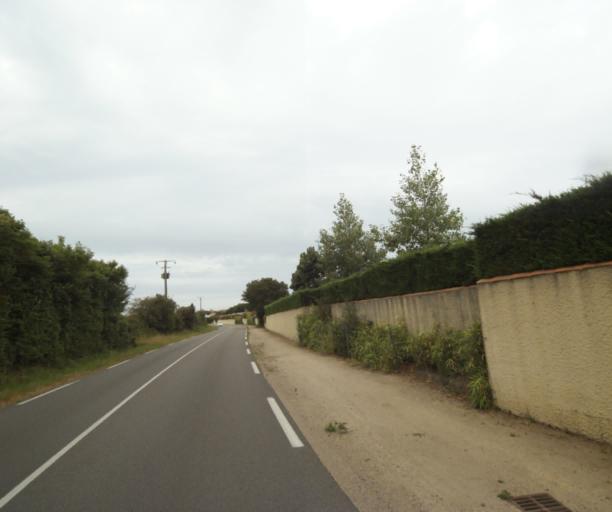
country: FR
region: Pays de la Loire
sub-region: Departement de la Vendee
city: Chateau-d'Olonne
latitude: 46.4724
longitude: -1.7230
